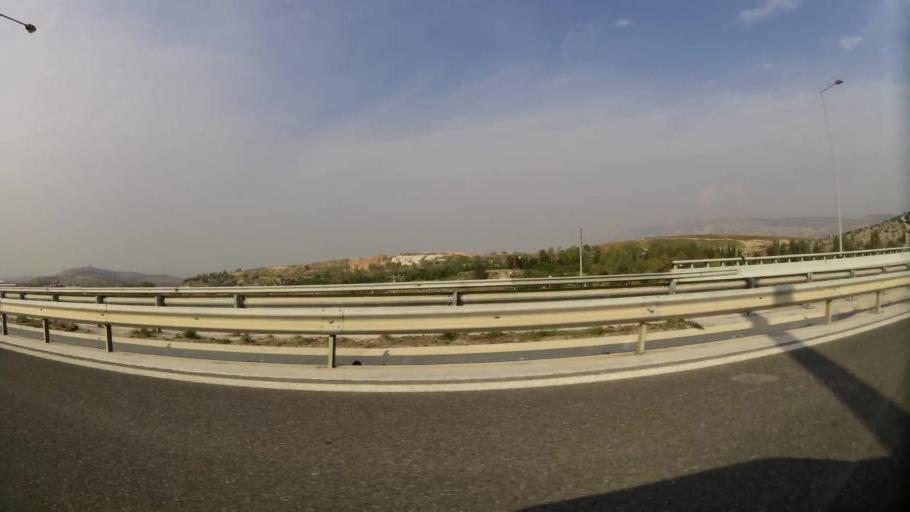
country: GR
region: Attica
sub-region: Nomarchia Athinas
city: Petroupolis
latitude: 38.0635
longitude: 23.6671
